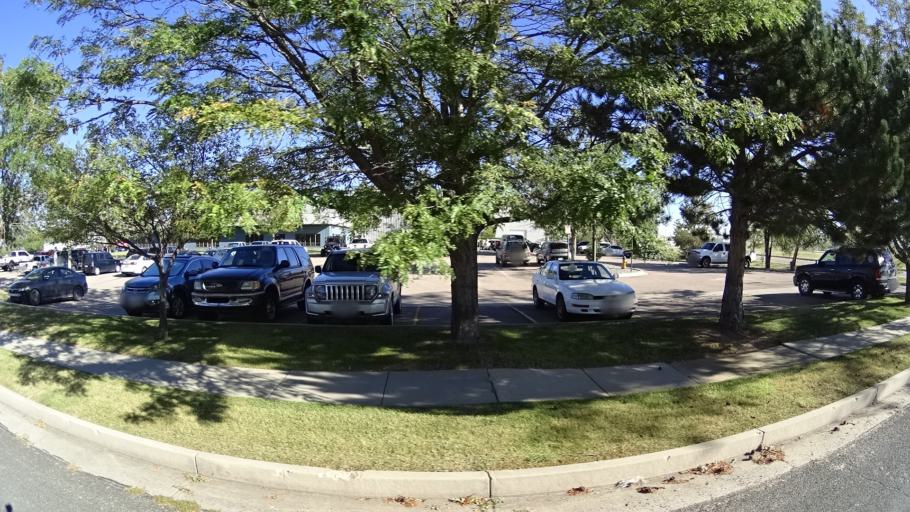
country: US
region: Colorado
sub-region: El Paso County
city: Cimarron Hills
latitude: 38.8143
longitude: -104.7241
